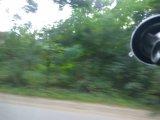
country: RU
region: Moskovskaya
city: Zhukovskiy
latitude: 55.5865
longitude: 38.1489
